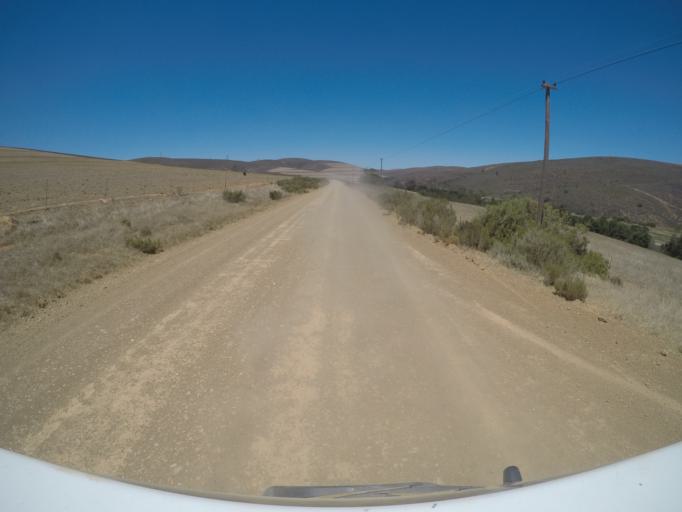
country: ZA
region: Western Cape
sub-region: Overberg District Municipality
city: Caledon
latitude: -34.1328
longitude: 19.2423
